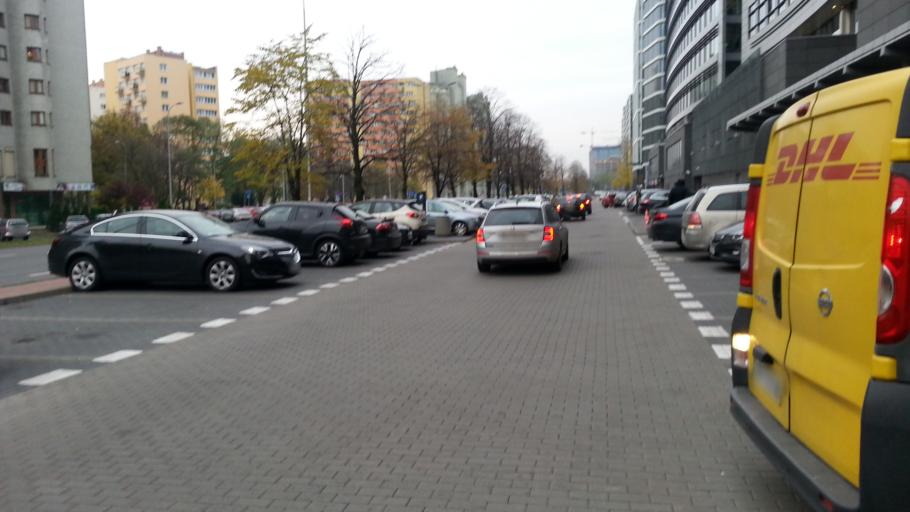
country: PL
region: Masovian Voivodeship
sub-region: Warszawa
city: Ochota
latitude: 52.2229
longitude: 20.9805
